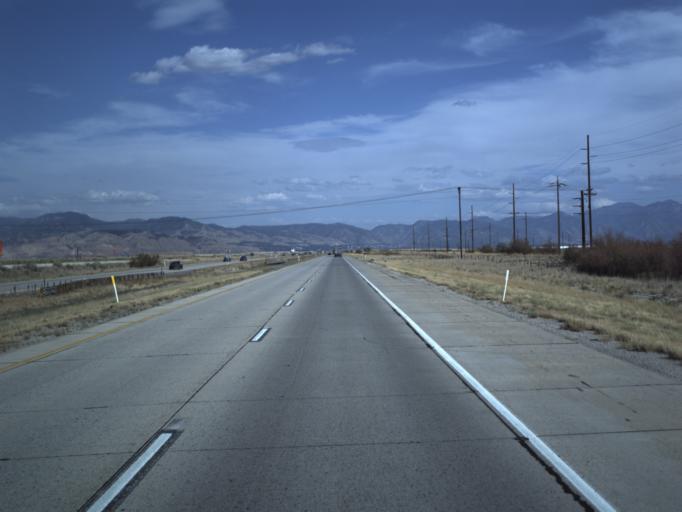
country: US
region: Utah
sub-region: Salt Lake County
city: Magna
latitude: 40.7708
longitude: -112.1024
